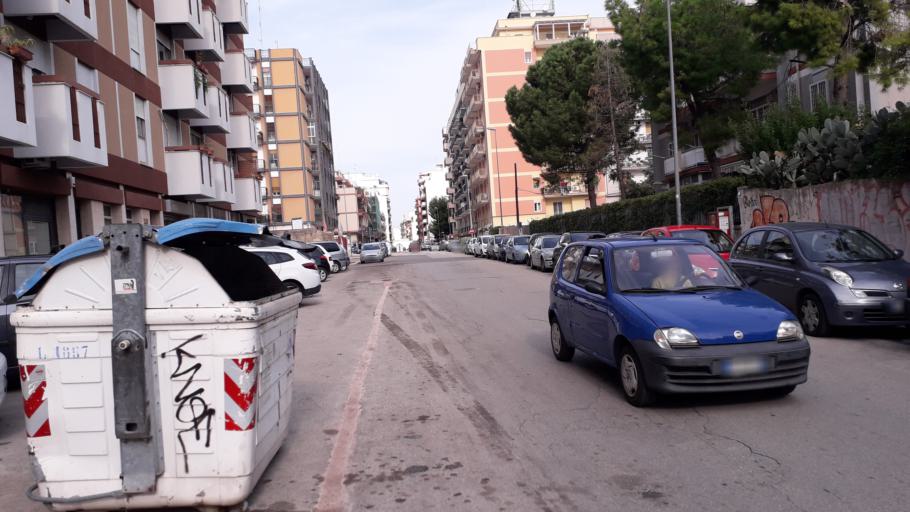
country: IT
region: Apulia
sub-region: Provincia di Bari
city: Bari
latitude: 41.1098
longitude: 16.8754
